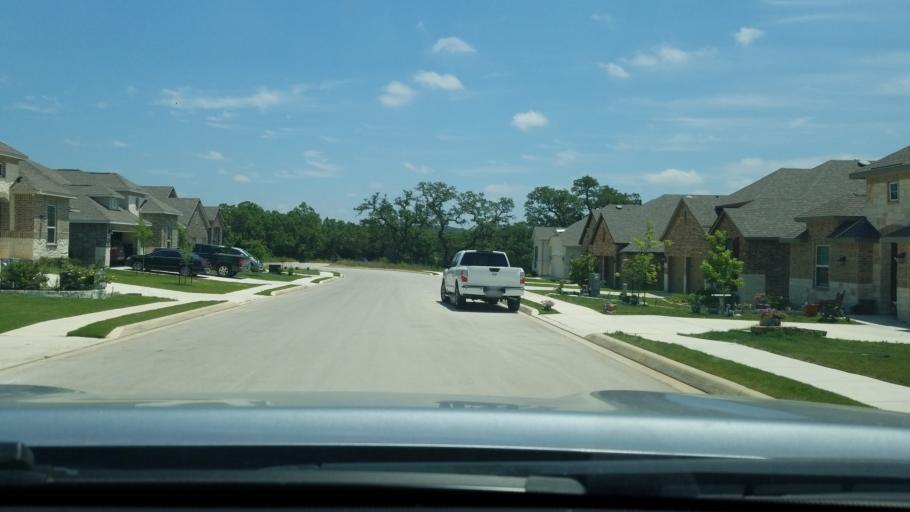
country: US
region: Texas
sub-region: Comal County
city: Bulverde
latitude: 29.8024
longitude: -98.5197
